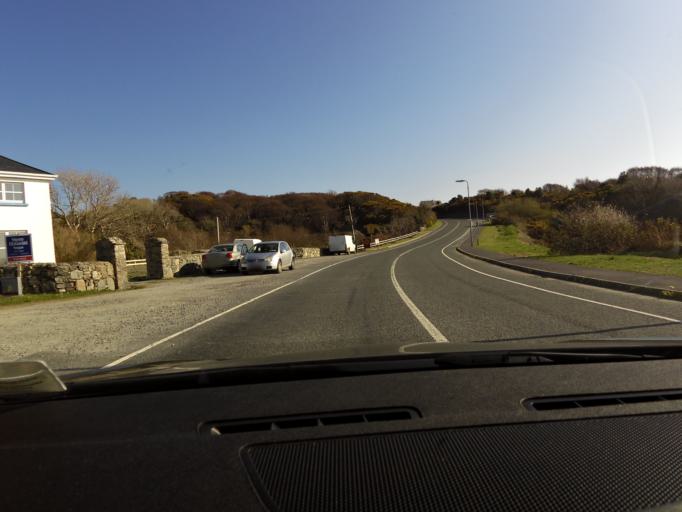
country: IE
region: Connaught
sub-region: County Galway
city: Clifden
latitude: 53.4849
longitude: -10.0242
